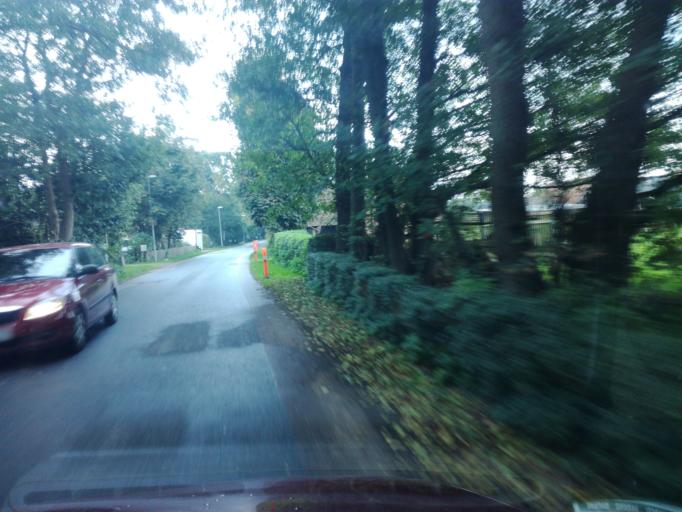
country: DK
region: South Denmark
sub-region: Fredericia Kommune
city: Fredericia
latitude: 55.6253
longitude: 9.8037
